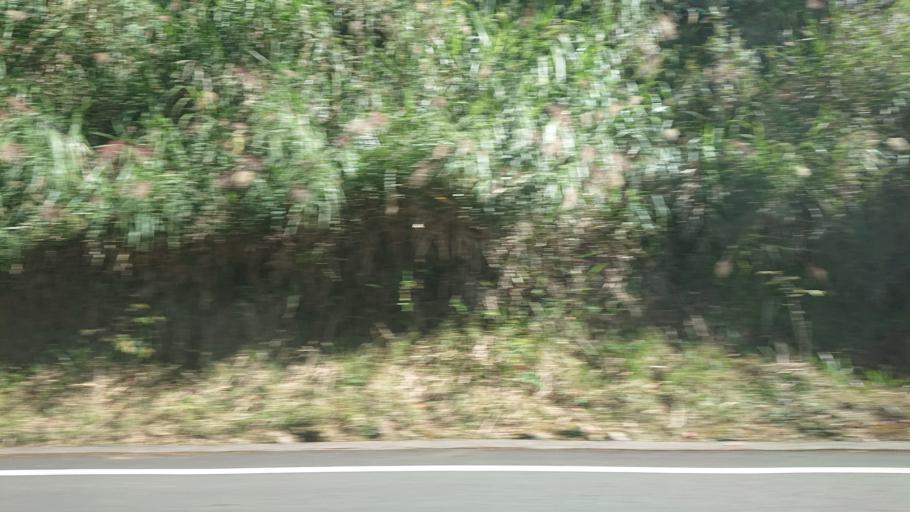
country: TW
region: Taiwan
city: Lugu
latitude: 23.5014
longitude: 120.8006
